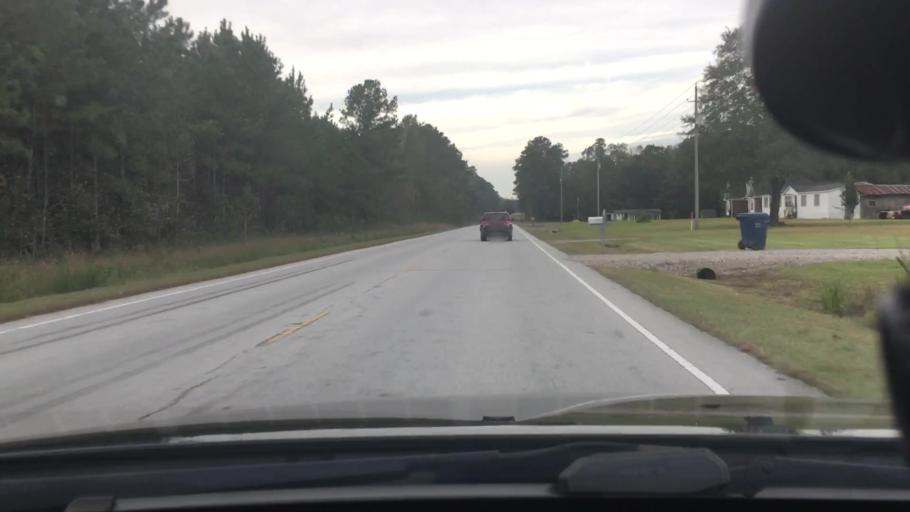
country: US
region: North Carolina
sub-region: Pitt County
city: Windsor
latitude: 35.4772
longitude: -77.2962
